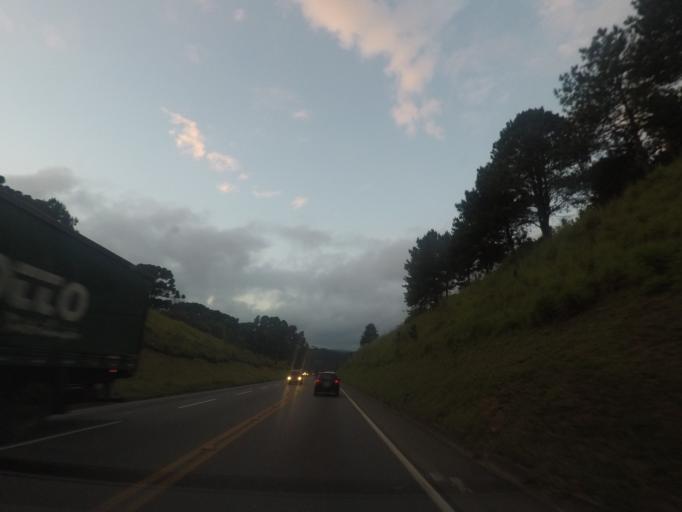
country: BR
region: Parana
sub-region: Almirante Tamandare
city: Almirante Tamandare
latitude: -25.4006
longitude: -49.3615
